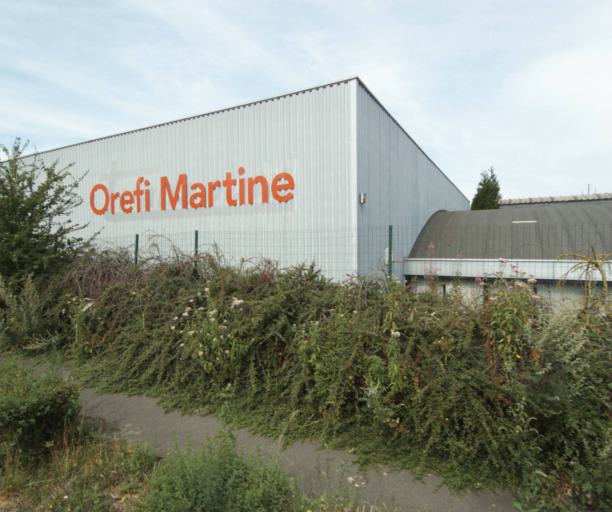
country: FR
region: Nord-Pas-de-Calais
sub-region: Departement du Nord
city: Mouvaux
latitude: 50.7192
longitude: 3.1278
